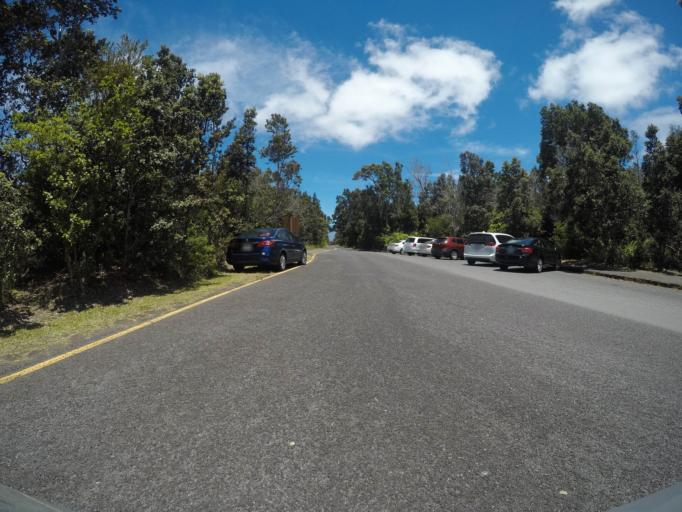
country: US
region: Hawaii
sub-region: Hawaii County
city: Volcano
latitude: 19.3653
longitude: -155.2165
